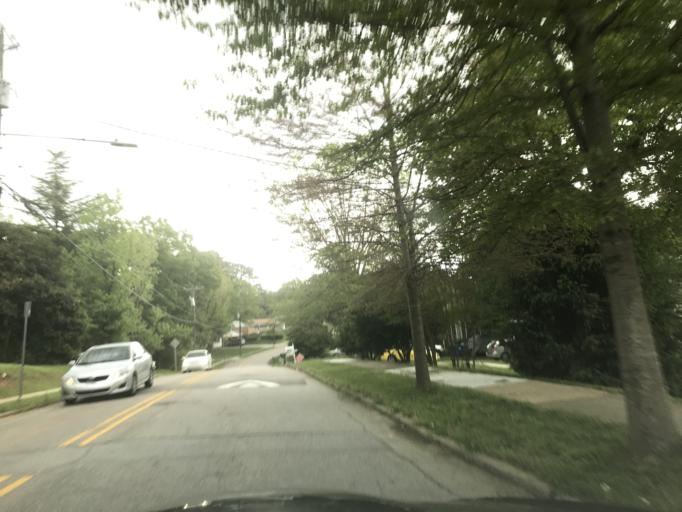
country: US
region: North Carolina
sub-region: Wake County
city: West Raleigh
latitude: 35.7768
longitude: -78.7071
